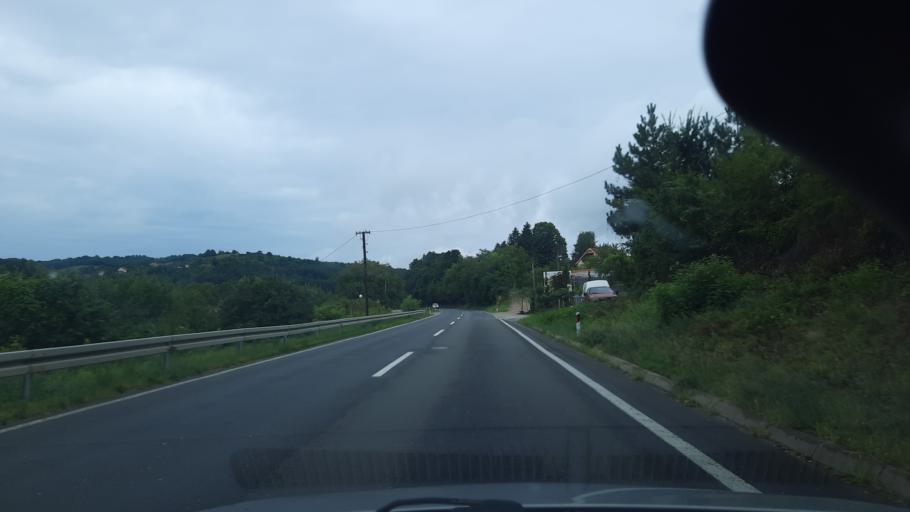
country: RS
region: Central Serbia
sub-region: Sumadijski Okrug
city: Knic
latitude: 43.9689
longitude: 20.8106
